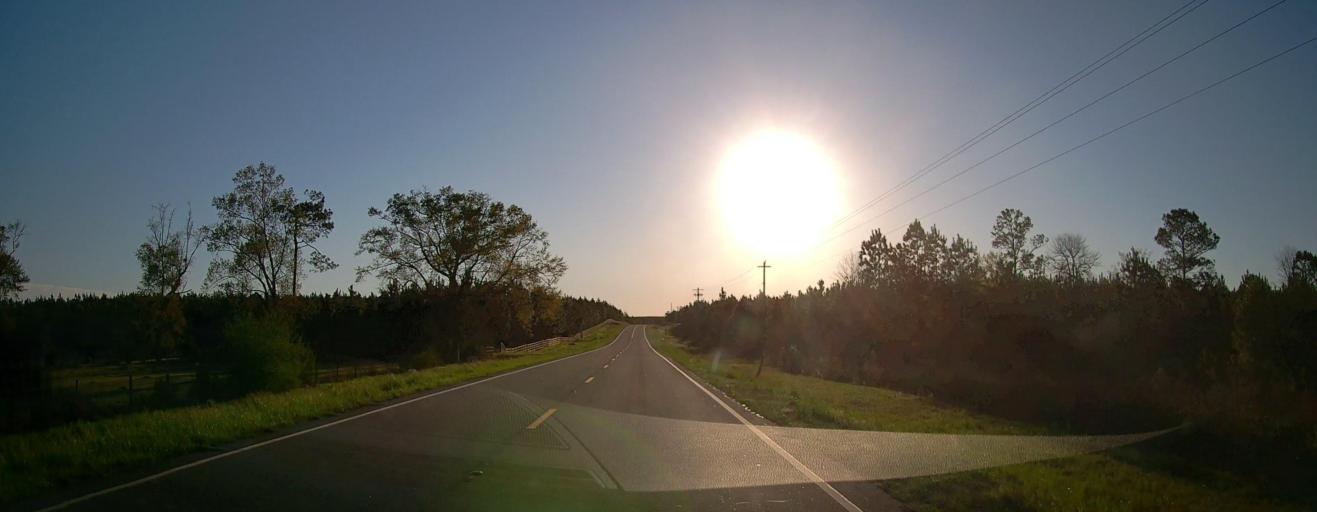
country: US
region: Georgia
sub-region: Wilcox County
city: Abbeville
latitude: 31.9899
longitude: -83.3261
